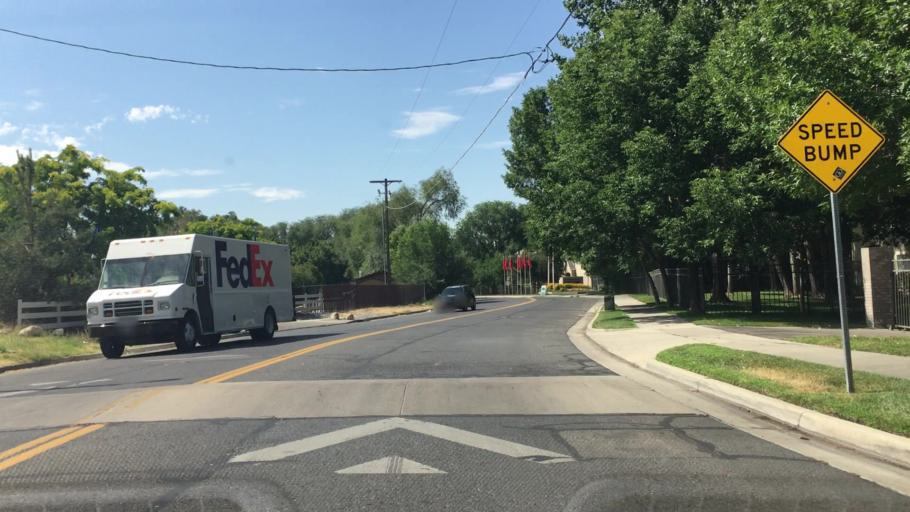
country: US
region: Utah
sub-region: Salt Lake County
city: Millcreek
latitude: 40.6822
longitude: -111.8828
